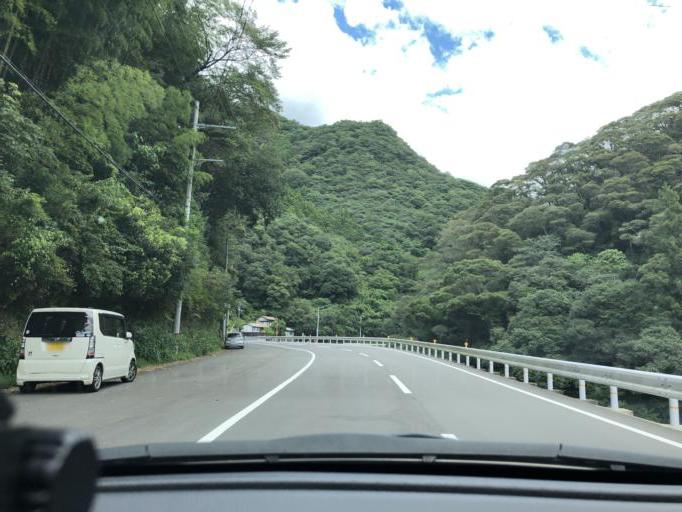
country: JP
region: Kochi
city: Kochi-shi
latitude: 33.6243
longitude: 133.4986
